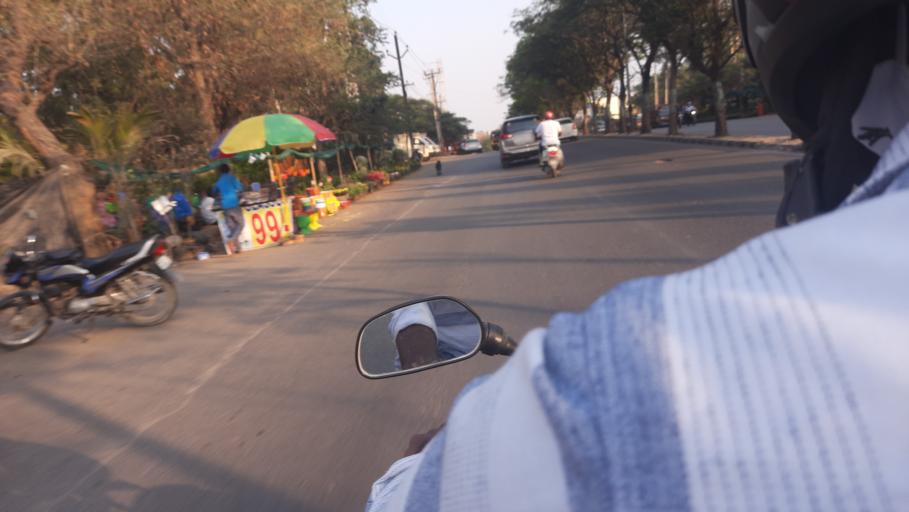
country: IN
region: Telangana
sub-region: Rangareddi
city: Secunderabad
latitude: 17.4836
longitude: 78.5500
